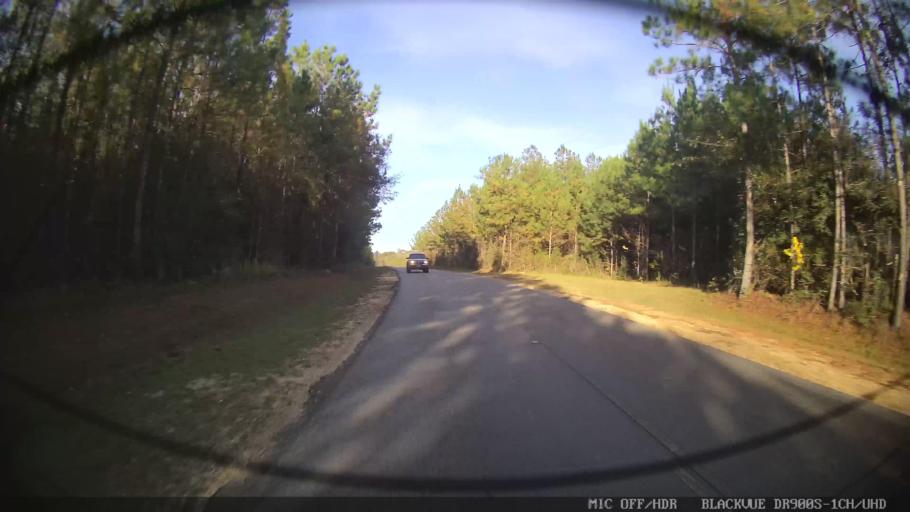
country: US
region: Mississippi
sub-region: Lamar County
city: Purvis
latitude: 31.1518
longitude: -89.3355
